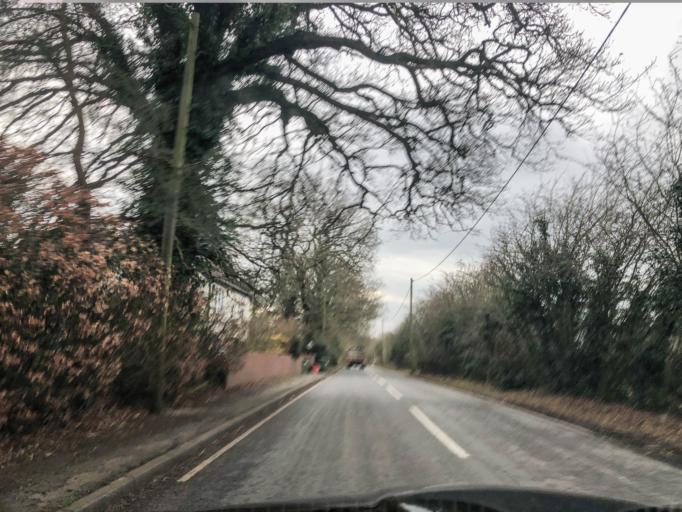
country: GB
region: England
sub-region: Warwickshire
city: Wroxall
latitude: 52.3266
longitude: -1.6677
